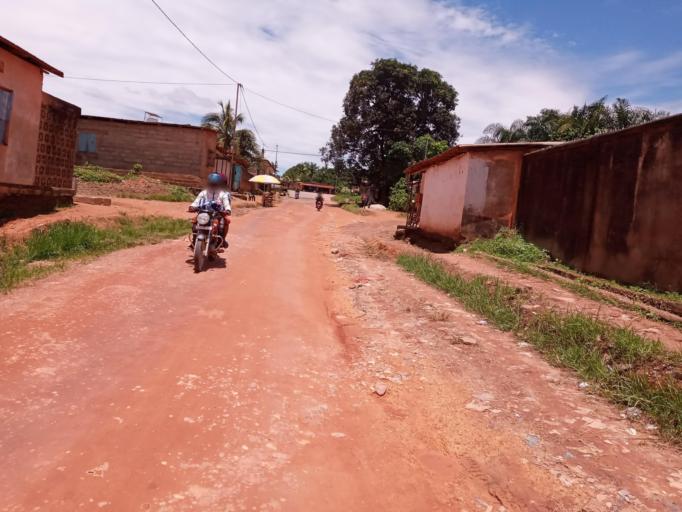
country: SL
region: Eastern Province
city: Koidu
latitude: 8.6452
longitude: -10.9626
